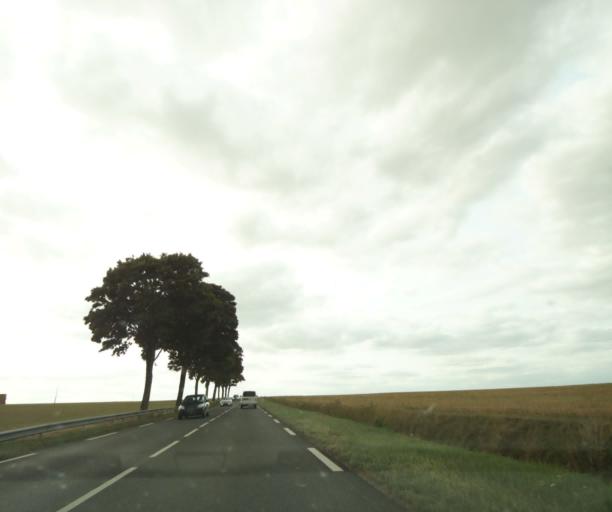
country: FR
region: Centre
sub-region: Departement d'Indre-et-Loire
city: Chambourg-sur-Indre
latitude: 47.1847
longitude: 0.9478
